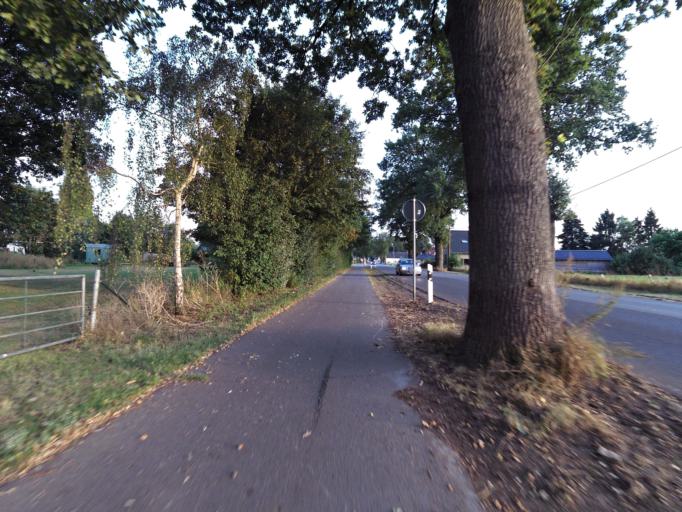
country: DE
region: North Rhine-Westphalia
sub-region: Regierungsbezirk Dusseldorf
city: Kleve
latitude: 51.8826
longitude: 6.1542
